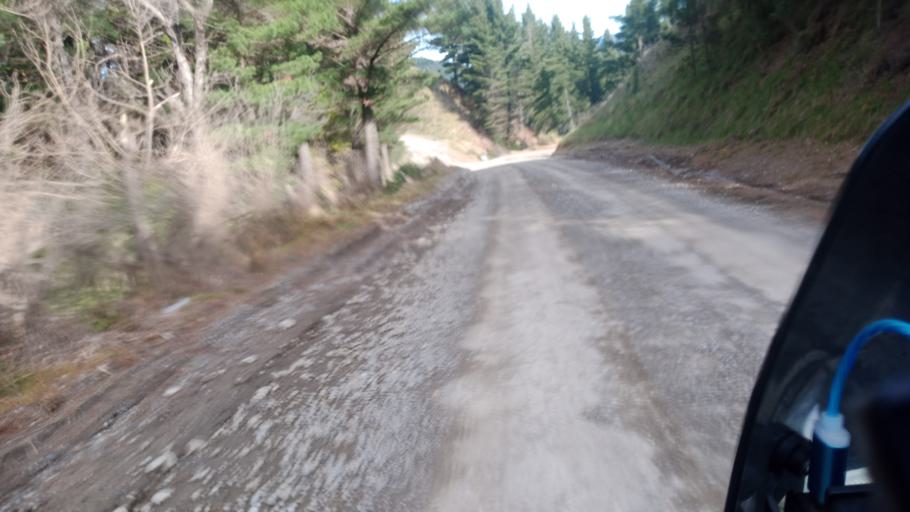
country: NZ
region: Gisborne
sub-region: Gisborne District
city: Gisborne
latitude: -38.1223
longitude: 178.1578
